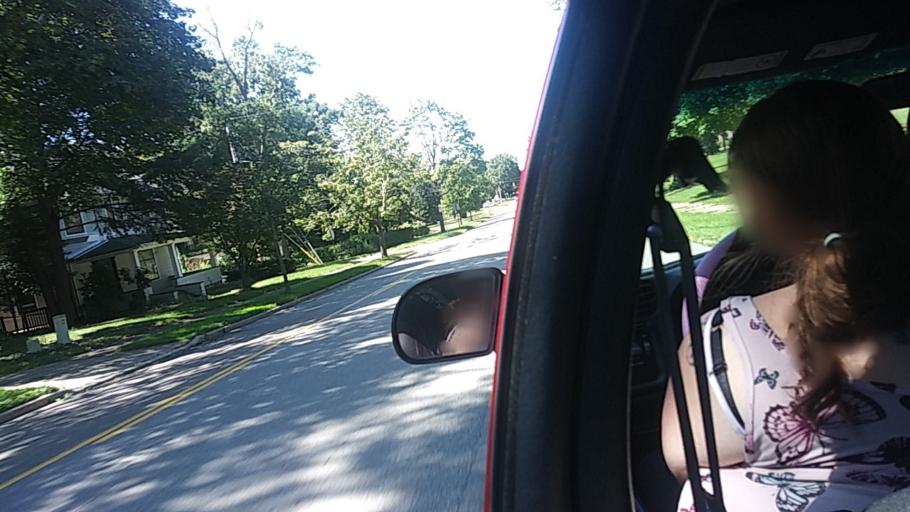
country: US
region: Ohio
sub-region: Summit County
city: Akron
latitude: 41.0975
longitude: -81.5533
